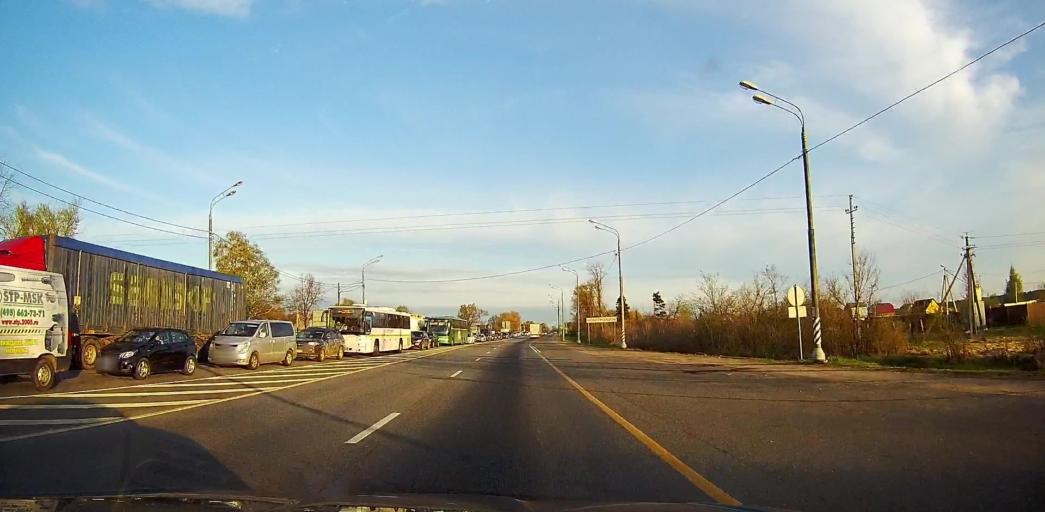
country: RU
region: Moskovskaya
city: Troitskoye
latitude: 55.2771
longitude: 38.4943
